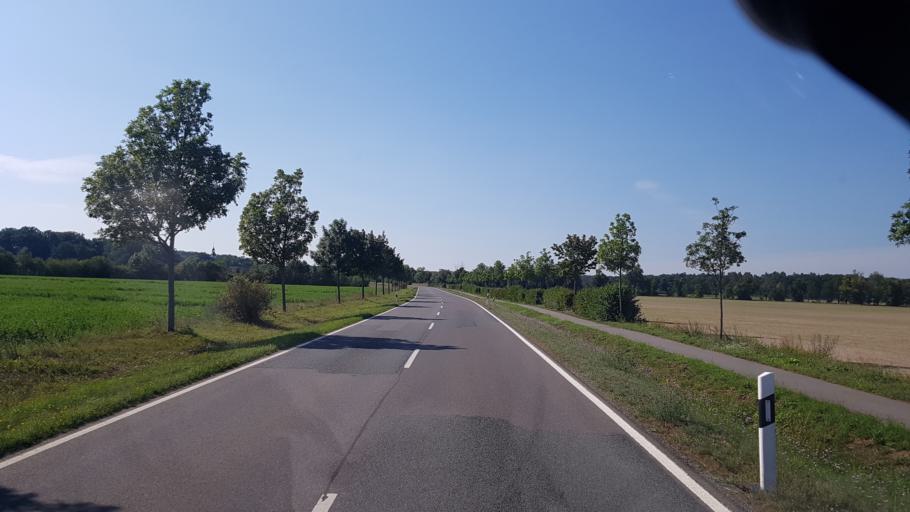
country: DE
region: Brandenburg
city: Altdobern
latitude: 51.7210
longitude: 14.0416
